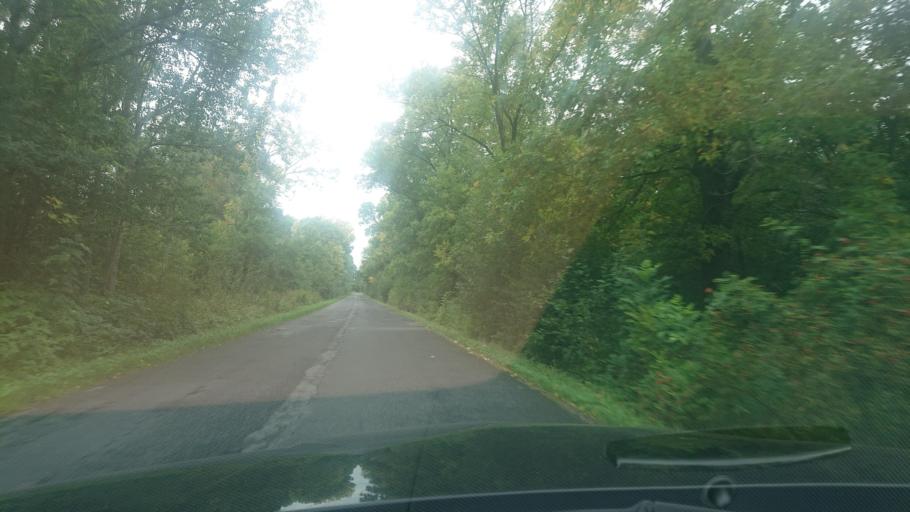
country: PL
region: Lower Silesian Voivodeship
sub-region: Powiat klodzki
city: Miedzylesie
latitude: 50.2250
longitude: 16.7238
